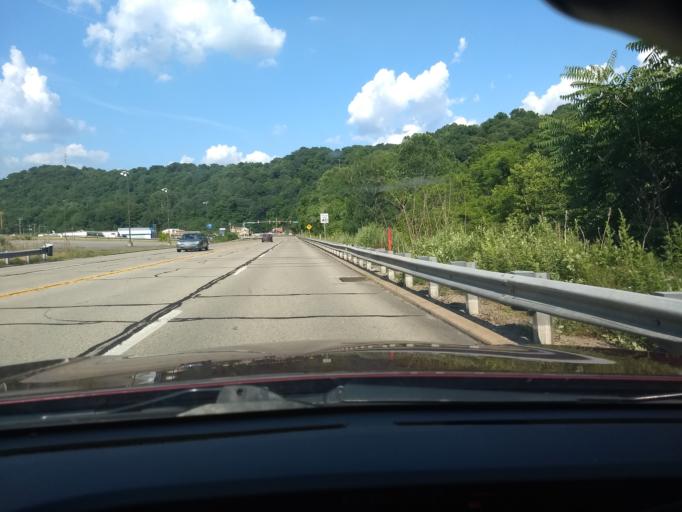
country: US
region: Pennsylvania
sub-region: Allegheny County
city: Versailles
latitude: 40.3227
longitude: -79.8229
